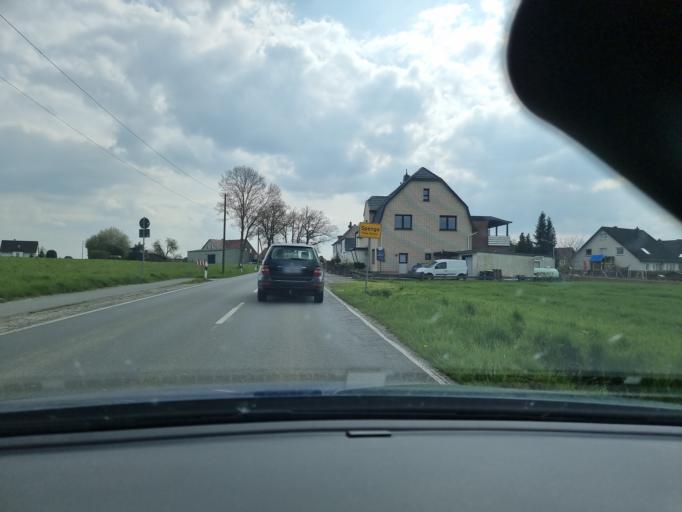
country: DE
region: North Rhine-Westphalia
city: Spenge
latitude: 52.1522
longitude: 8.4955
